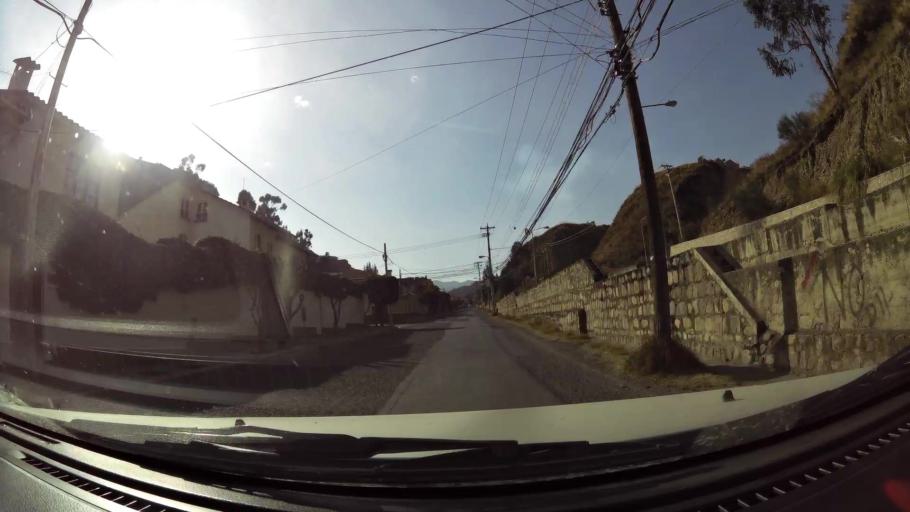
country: BO
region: La Paz
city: La Paz
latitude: -16.5279
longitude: -68.0782
